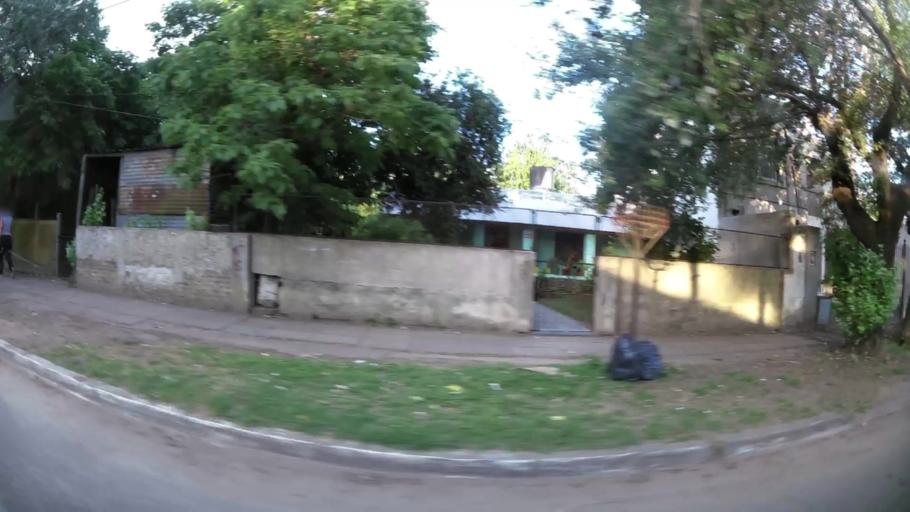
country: AR
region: Buenos Aires
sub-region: Partido de Merlo
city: Merlo
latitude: -34.6752
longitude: -58.7656
